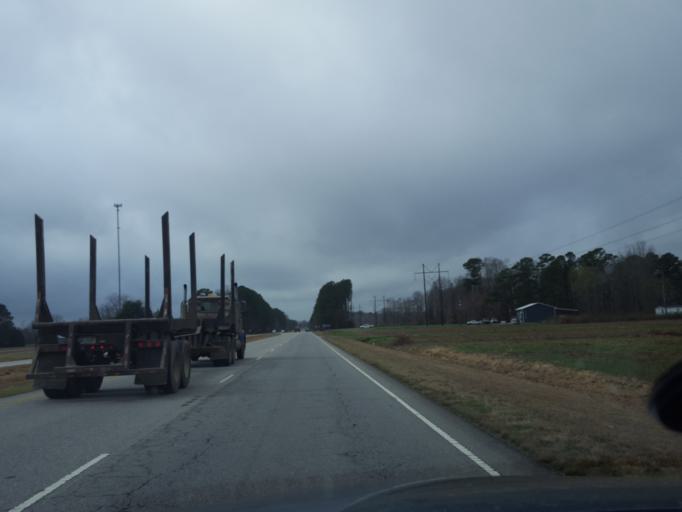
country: US
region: North Carolina
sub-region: Washington County
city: Plymouth
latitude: 35.8289
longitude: -76.8177
